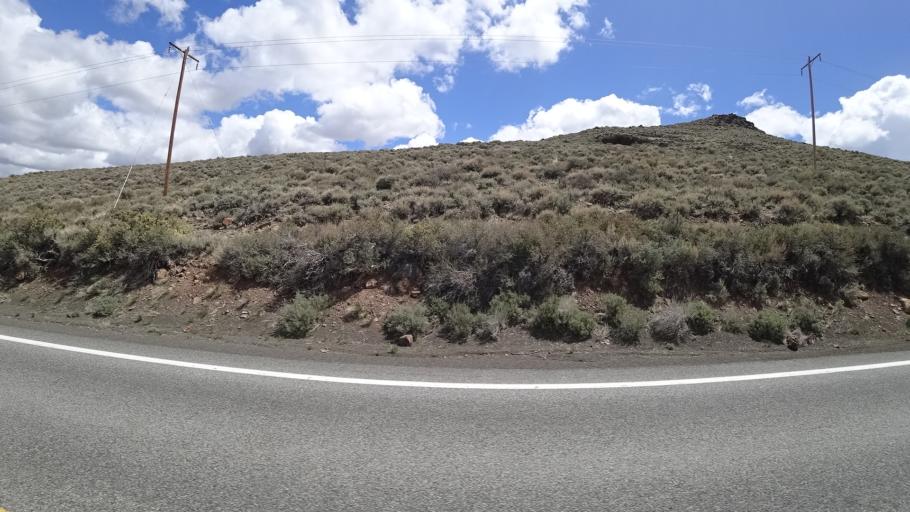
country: US
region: California
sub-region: Mono County
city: Bridgeport
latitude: 38.1440
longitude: -119.1849
